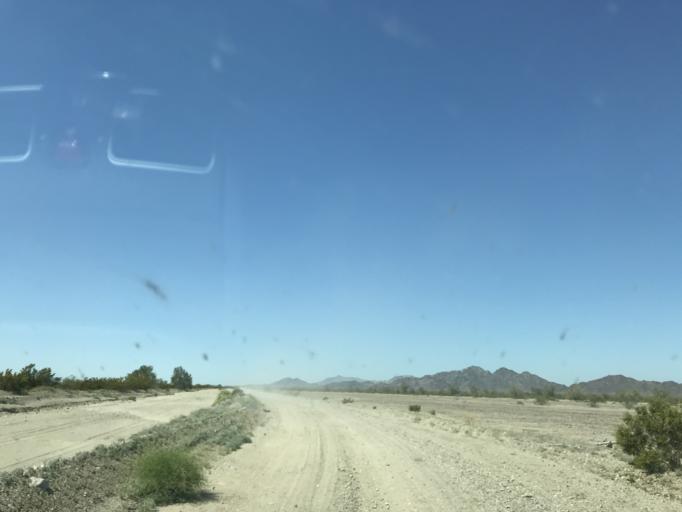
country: US
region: California
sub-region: Riverside County
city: Mesa Verde
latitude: 33.4893
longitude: -114.8956
